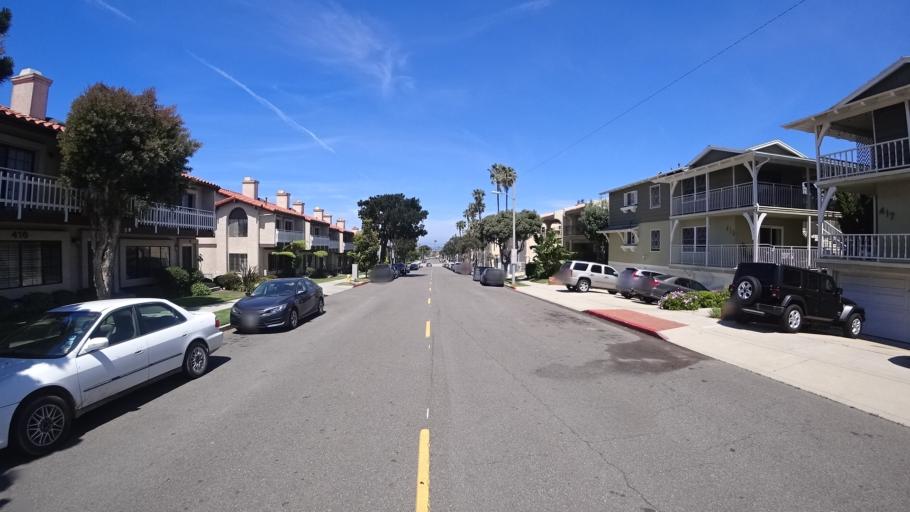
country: US
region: California
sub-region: Los Angeles County
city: Palos Verdes Estates
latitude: 33.8191
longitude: -118.3812
